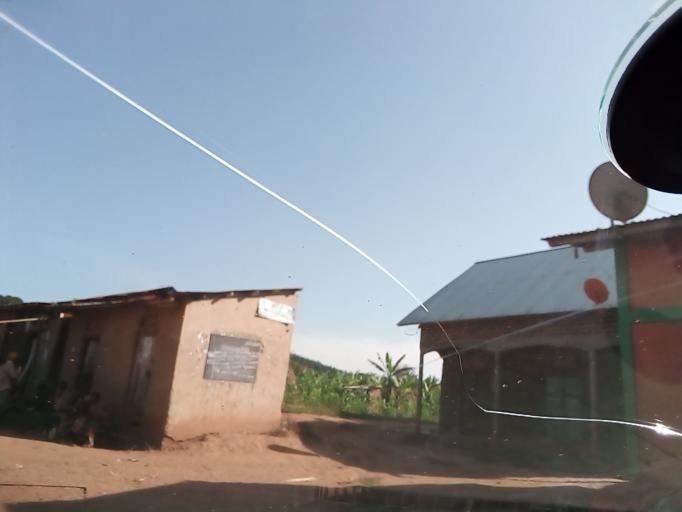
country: UG
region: Central Region
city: Masaka
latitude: -0.2692
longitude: 31.7218
